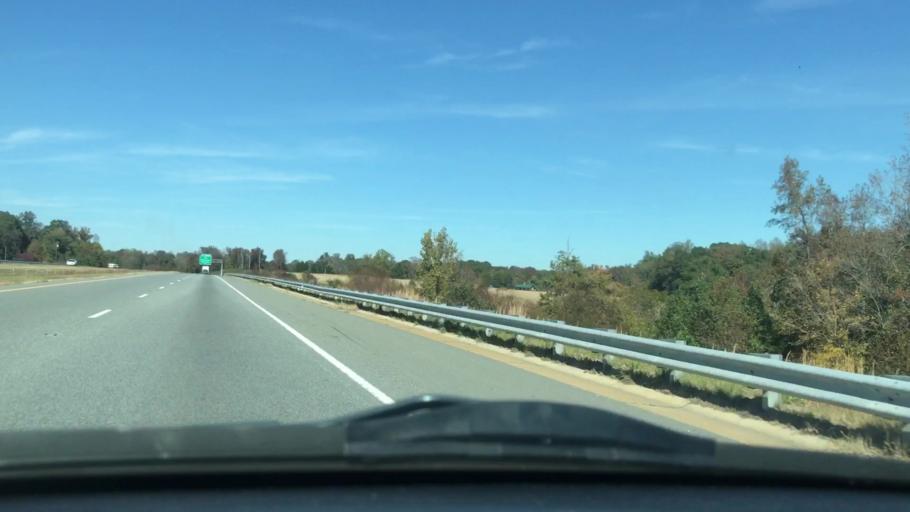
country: US
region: North Carolina
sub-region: Randolph County
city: Archdale
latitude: 35.9078
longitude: -79.9124
